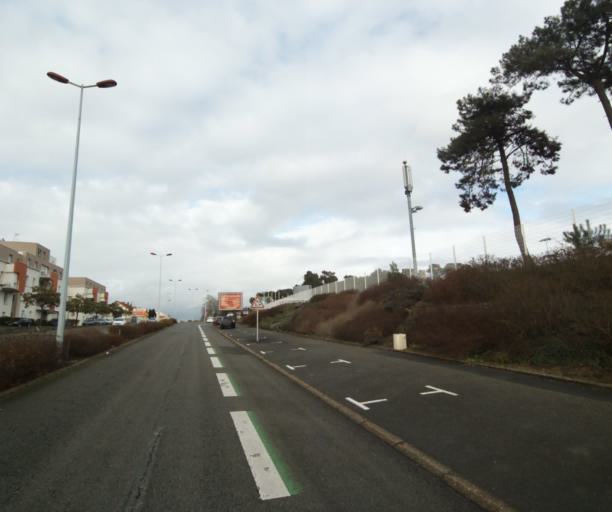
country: FR
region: Pays de la Loire
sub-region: Departement de la Sarthe
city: Arnage
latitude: 47.9590
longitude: 0.1993
